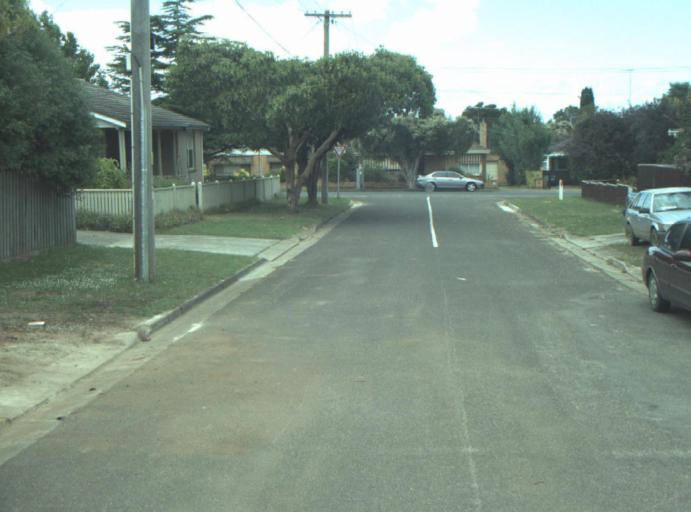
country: AU
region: Victoria
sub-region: Greater Geelong
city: Wandana Heights
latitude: -38.1816
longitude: 144.3159
